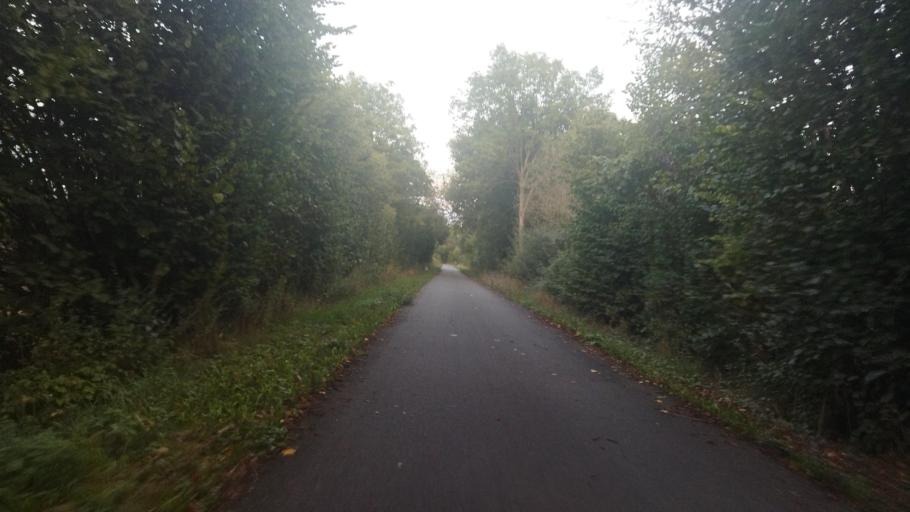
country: DE
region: North Rhine-Westphalia
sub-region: Regierungsbezirk Munster
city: Horstmar
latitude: 52.0300
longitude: 7.2967
